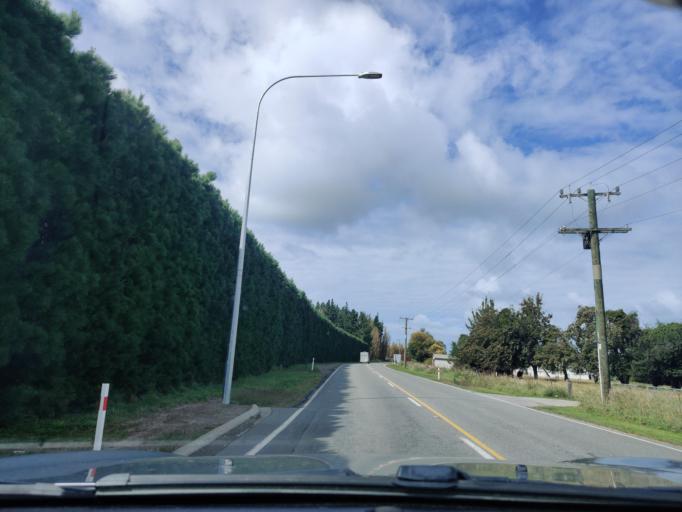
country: NZ
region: Canterbury
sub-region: Hurunui District
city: Amberley
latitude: -43.1589
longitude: 172.6945
